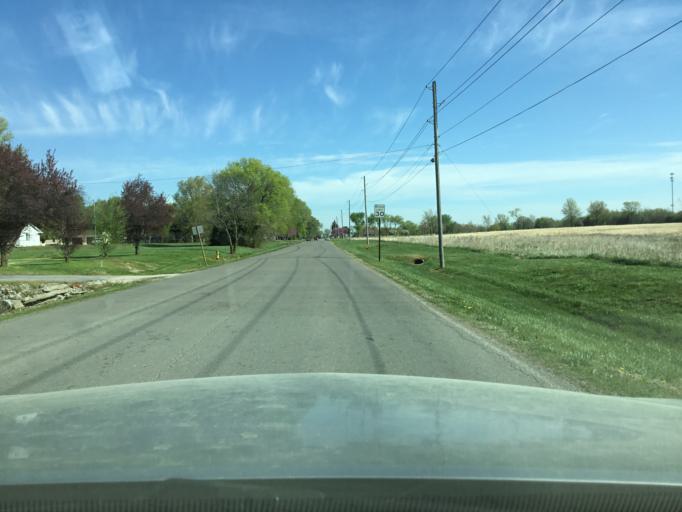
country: US
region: Kansas
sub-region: Neosho County
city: Chanute
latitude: 37.6605
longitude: -95.4435
